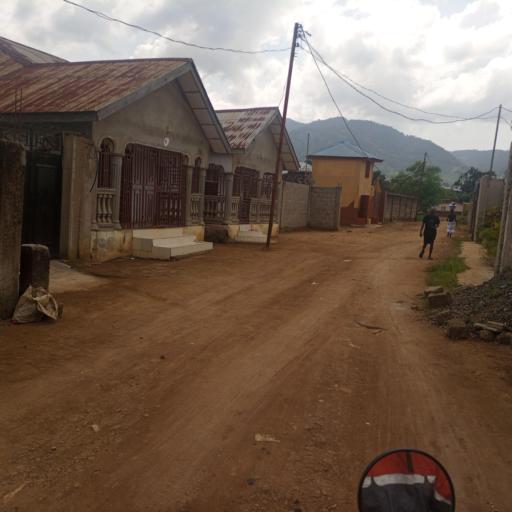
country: SL
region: Western Area
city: Hastings
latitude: 8.3858
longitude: -13.1428
